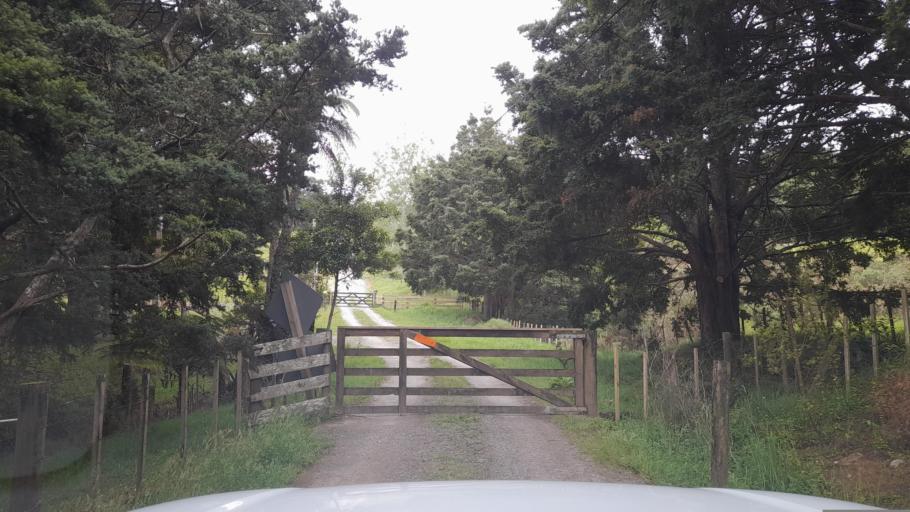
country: NZ
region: Northland
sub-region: Far North District
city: Waimate North
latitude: -35.3945
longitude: 173.7836
